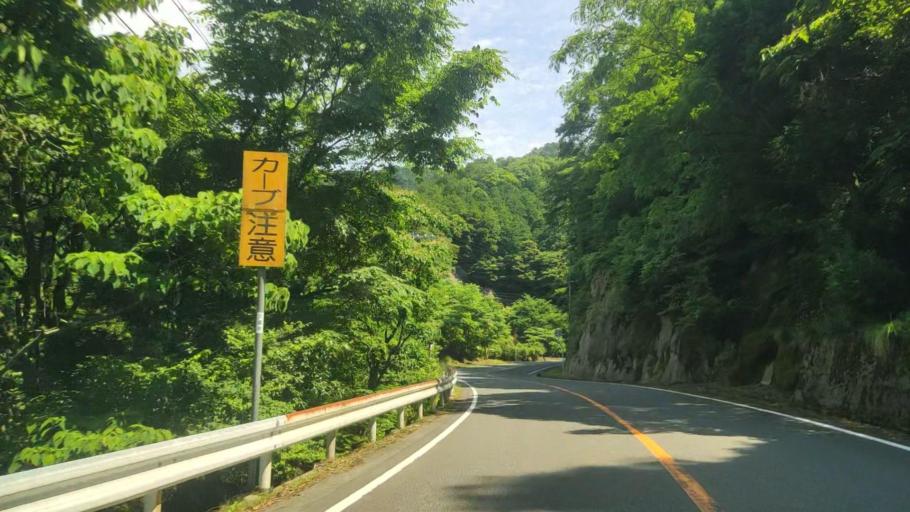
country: JP
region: Hyogo
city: Toyooka
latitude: 35.6350
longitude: 134.7805
